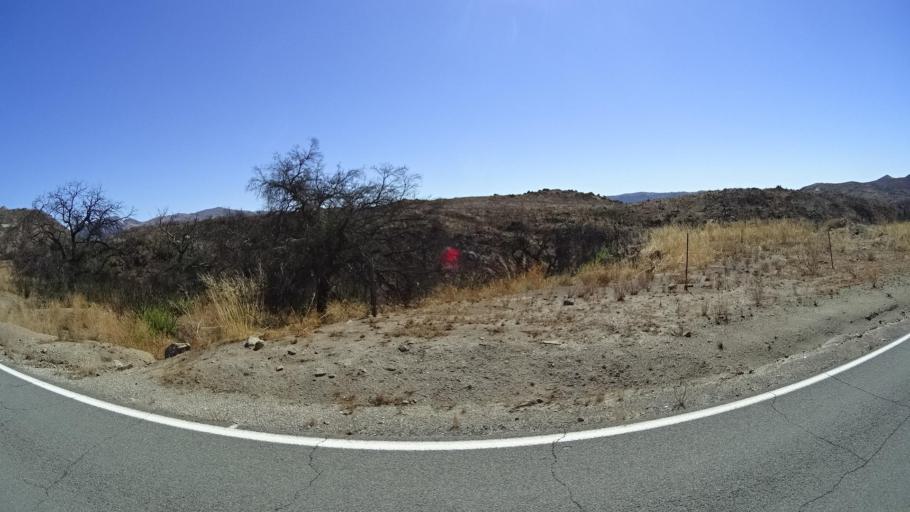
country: US
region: California
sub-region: San Diego County
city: Alpine
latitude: 32.7327
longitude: -116.6935
